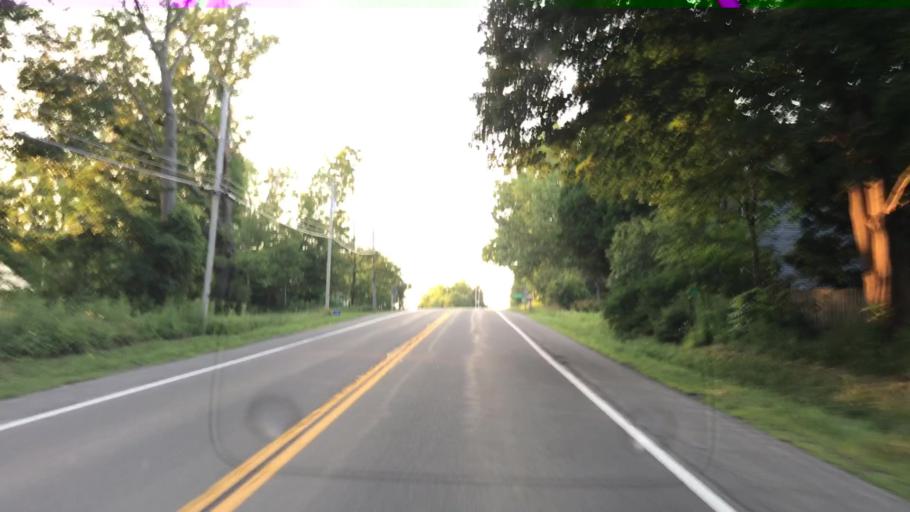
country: US
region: New York
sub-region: Chautauqua County
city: Mayville
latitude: 42.2570
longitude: -79.4679
